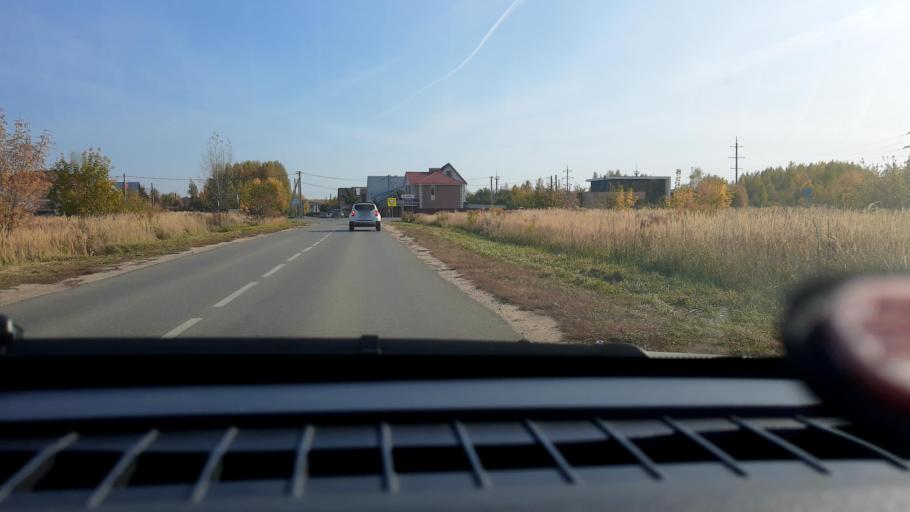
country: RU
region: Nizjnij Novgorod
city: Kstovo
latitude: 56.1475
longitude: 44.2291
